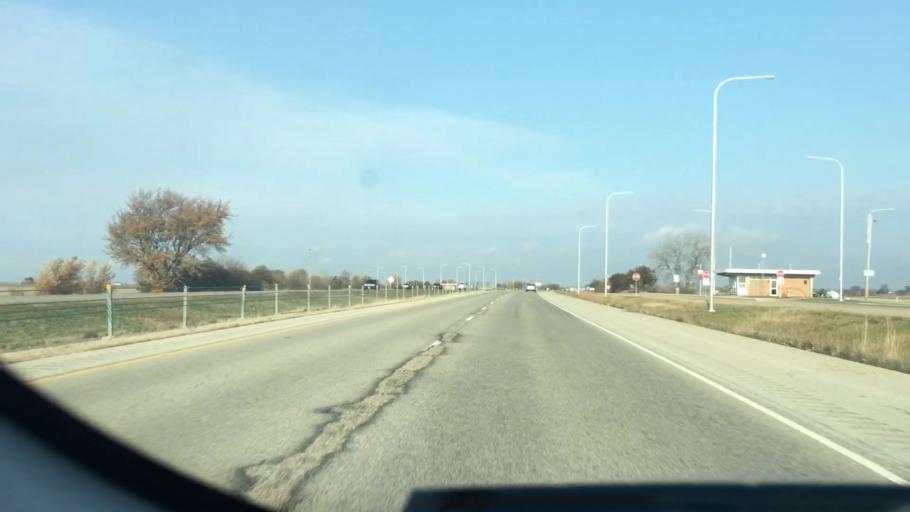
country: US
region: Illinois
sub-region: McLean County
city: Twin Grove
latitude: 40.5550
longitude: -89.1024
